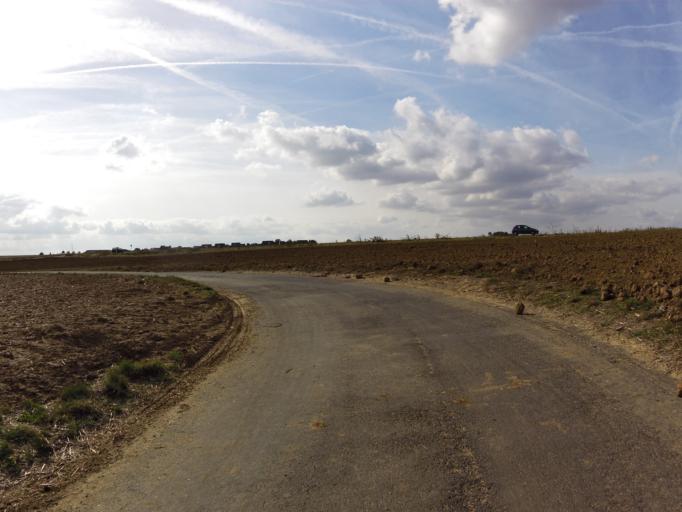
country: DE
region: Bavaria
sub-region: Regierungsbezirk Unterfranken
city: Reichenberg
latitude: 49.6998
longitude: 9.9404
